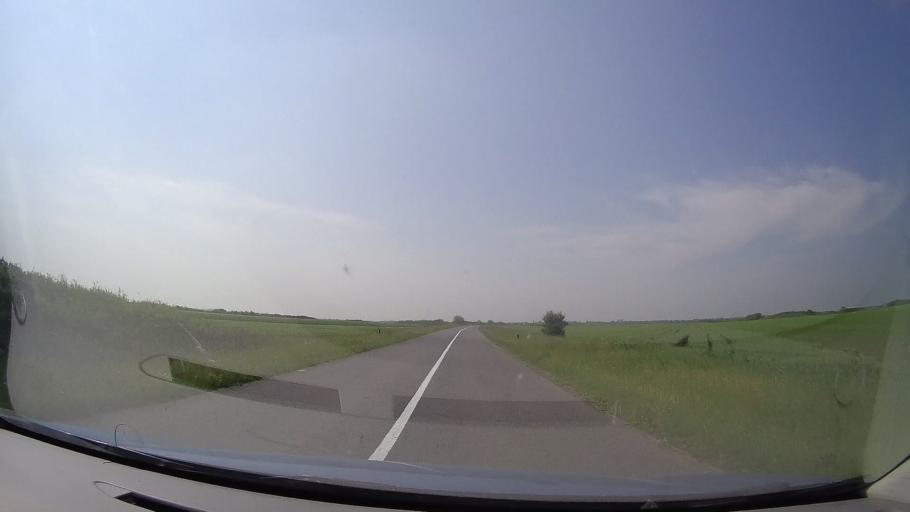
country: RS
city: Jarkovac
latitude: 45.2955
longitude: 20.7639
